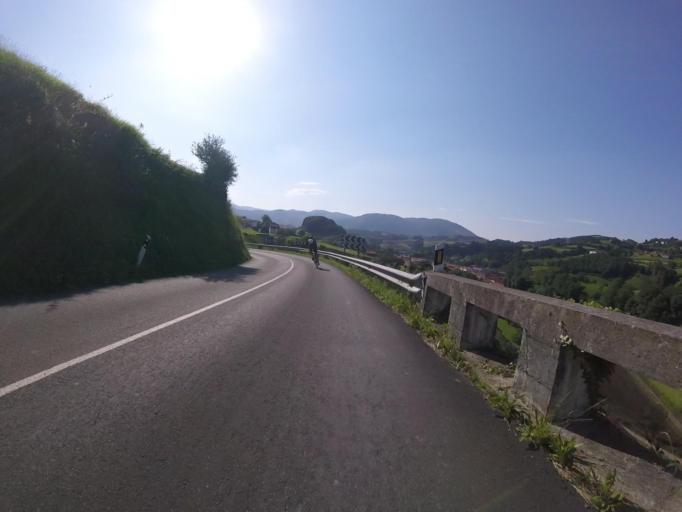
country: ES
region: Basque Country
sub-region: Provincia de Guipuzcoa
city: Asteasu
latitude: 43.1975
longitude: -2.1021
